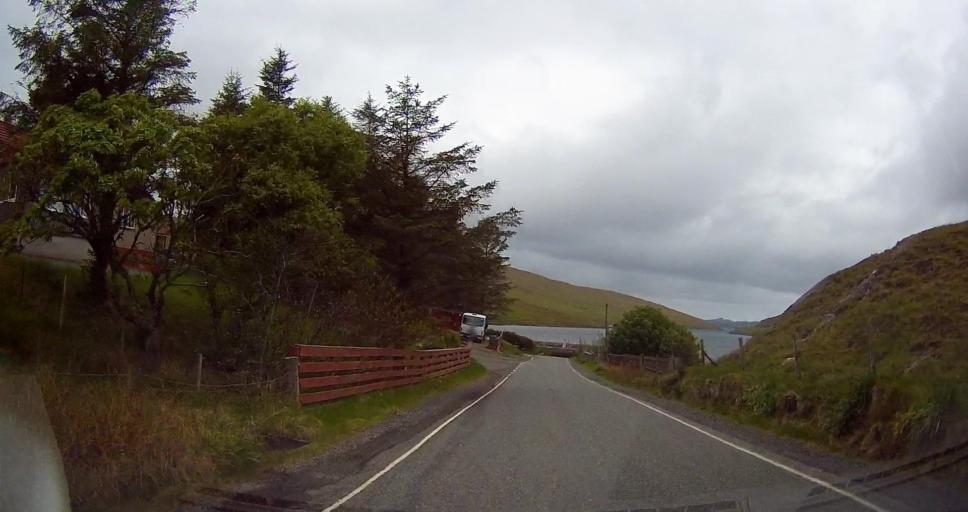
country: GB
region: Scotland
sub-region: Shetland Islands
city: Lerwick
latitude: 60.3504
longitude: -1.2608
